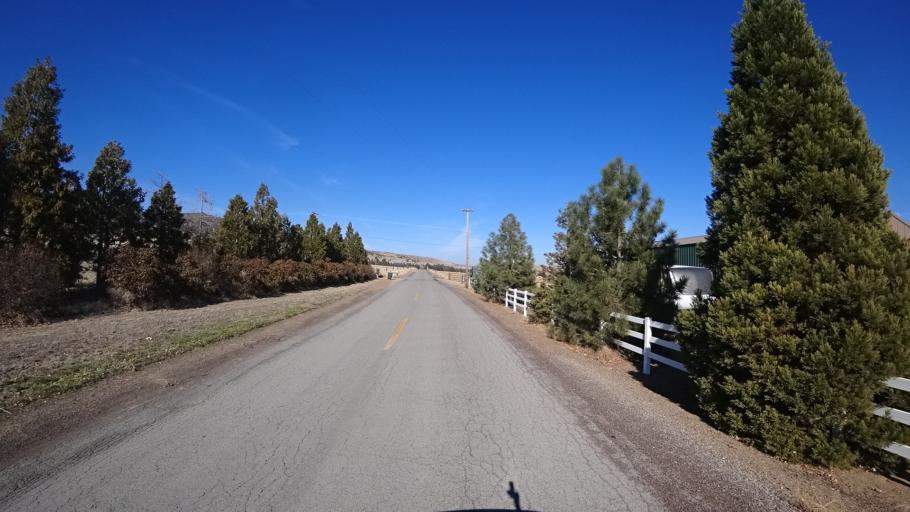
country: US
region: California
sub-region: Siskiyou County
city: Montague
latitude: 41.5848
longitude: -122.5443
